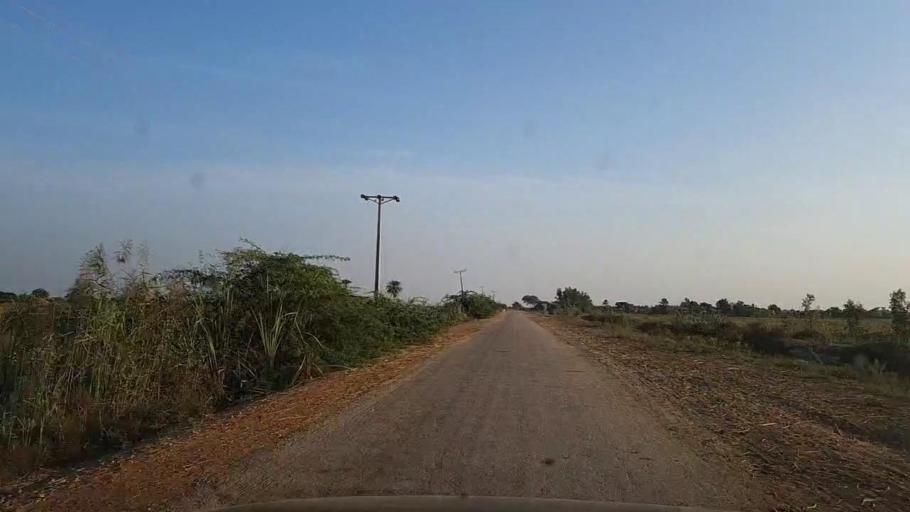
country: PK
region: Sindh
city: Thatta
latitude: 24.6285
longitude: 67.9133
